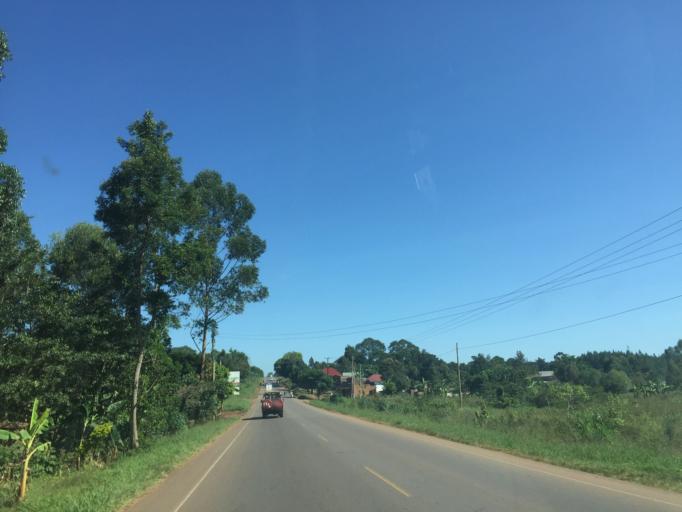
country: UG
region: Central Region
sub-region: Luwero District
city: Wobulenzi
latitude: 0.7439
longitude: 32.5165
